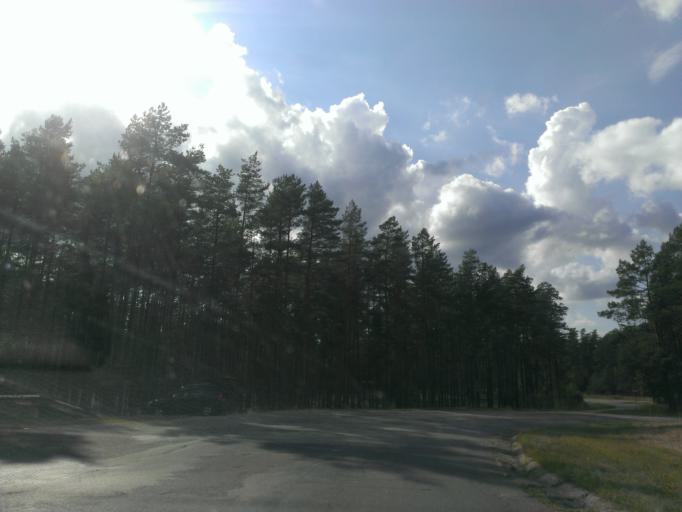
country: LV
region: Incukalns
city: Vangazi
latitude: 57.0785
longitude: 24.5229
